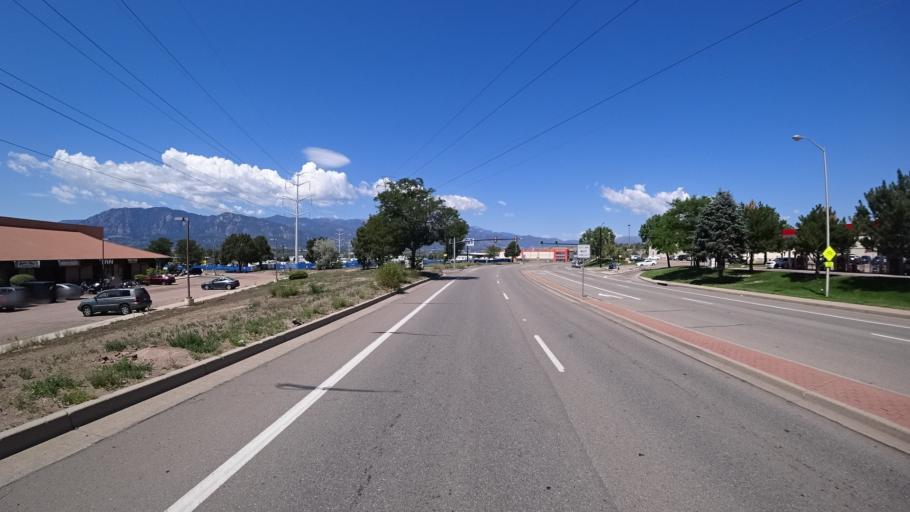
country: US
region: Colorado
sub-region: El Paso County
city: Stratmoor
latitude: 38.7891
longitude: -104.7598
